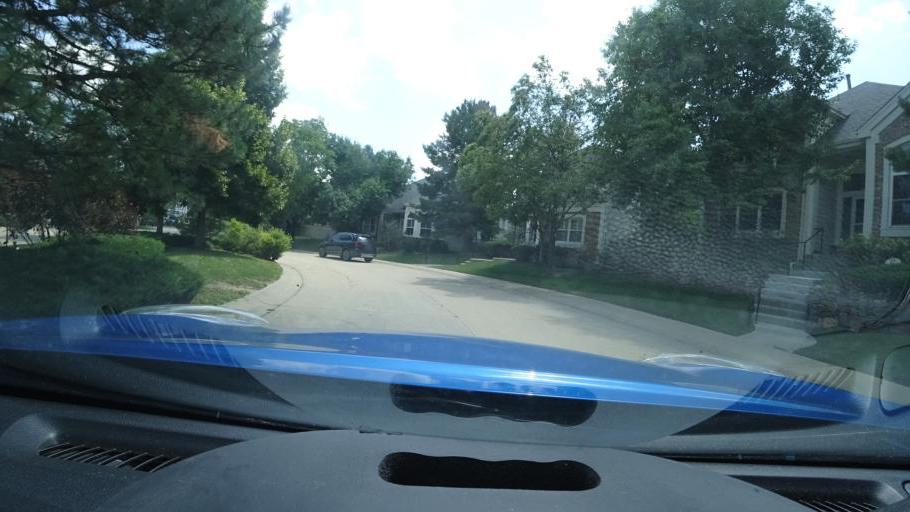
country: US
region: Colorado
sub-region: Arapahoe County
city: Glendale
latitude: 39.6994
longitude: -104.8935
